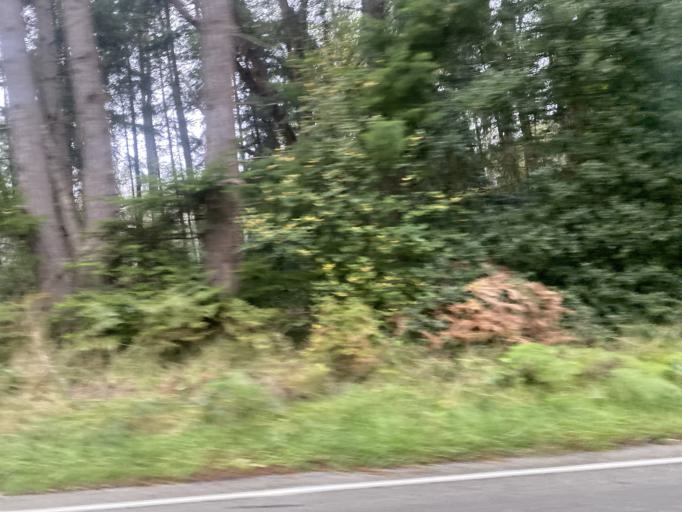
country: US
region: Washington
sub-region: Island County
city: Freeland
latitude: 48.0804
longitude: -122.4895
